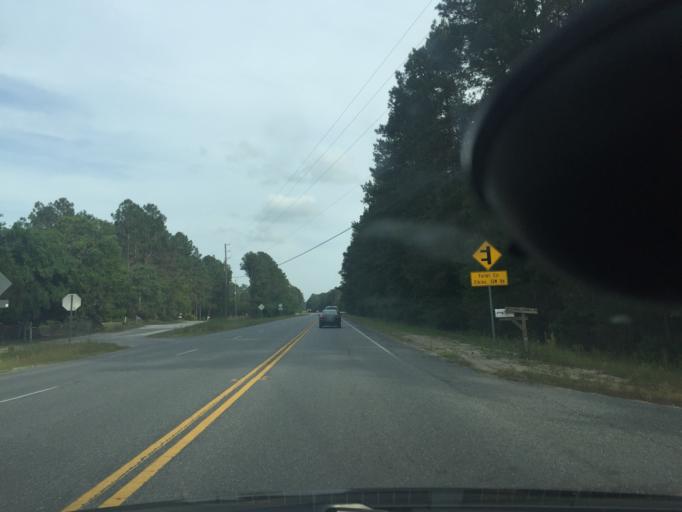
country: US
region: Georgia
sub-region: Chatham County
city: Bloomingdale
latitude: 32.0493
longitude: -81.3394
